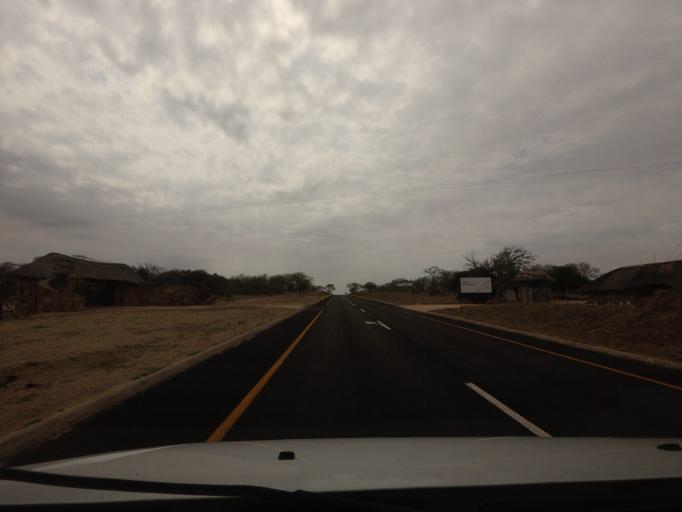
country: ZA
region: Limpopo
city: Thulamahashi
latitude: -24.5560
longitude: 31.2229
